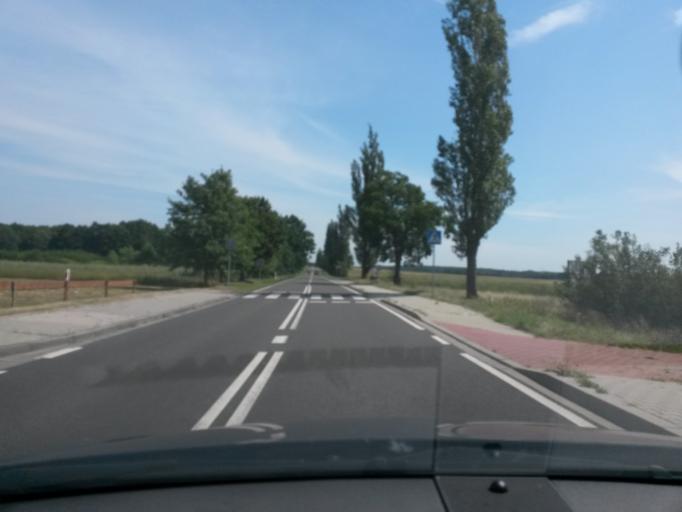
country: PL
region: Lower Silesian Voivodeship
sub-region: Powiat wolowski
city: Winsko
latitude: 51.4575
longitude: 16.5490
